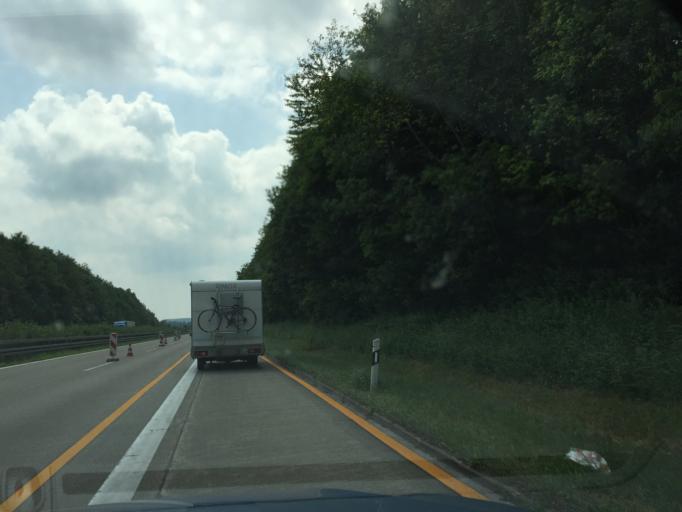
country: DE
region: Baden-Wuerttemberg
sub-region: Regierungsbezirk Stuttgart
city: Herbrechtingen
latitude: 48.6094
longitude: 10.2024
